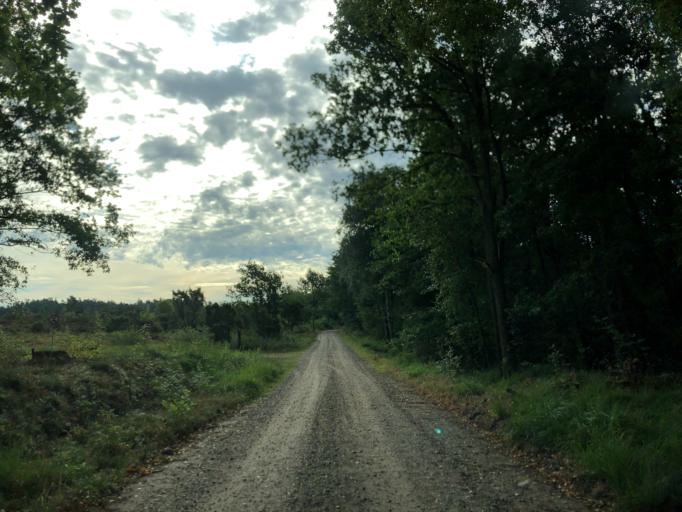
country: DK
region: Central Jutland
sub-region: Holstebro Kommune
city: Ulfborg
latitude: 56.1679
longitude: 8.3926
